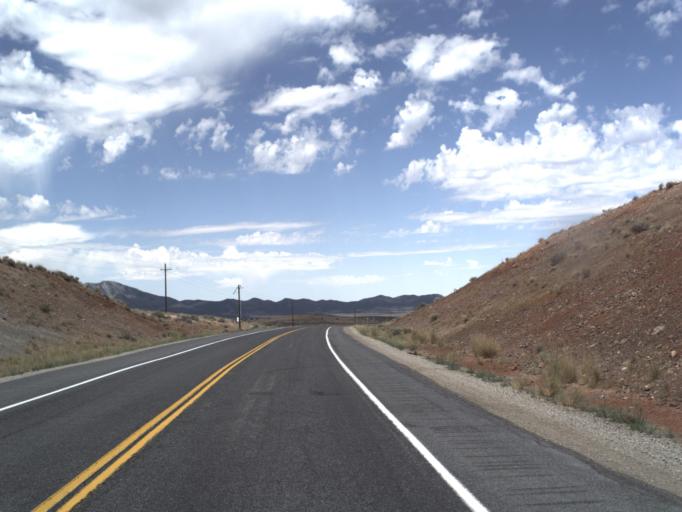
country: US
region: Utah
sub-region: Utah County
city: Eagle Mountain
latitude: 40.0720
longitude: -112.3678
